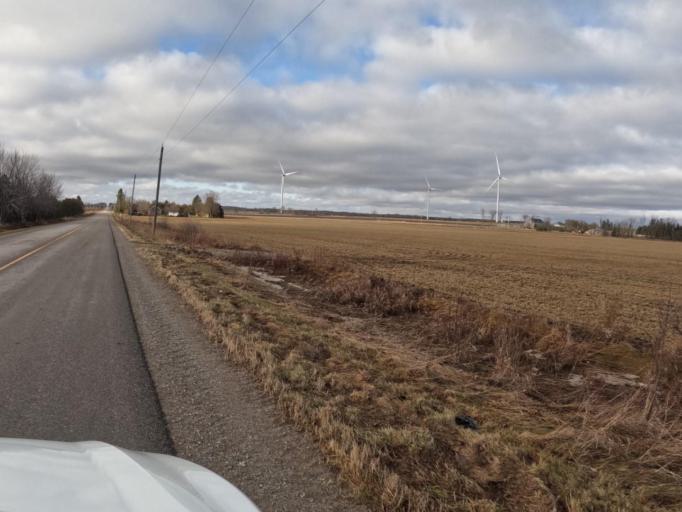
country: CA
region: Ontario
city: Shelburne
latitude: 43.8907
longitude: -80.3551
